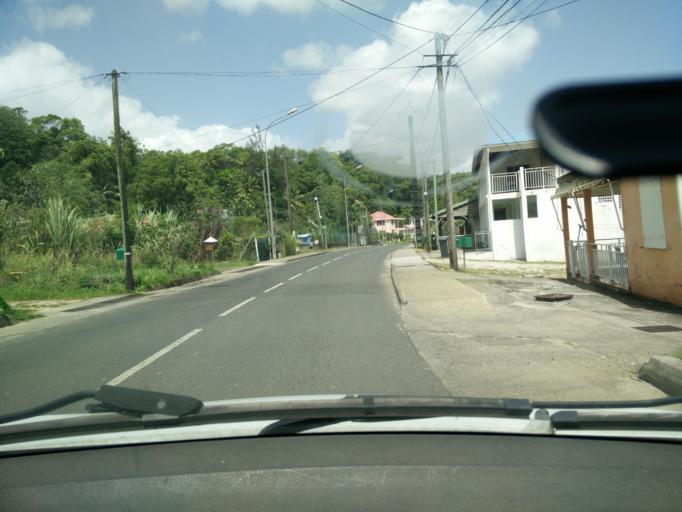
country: GP
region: Guadeloupe
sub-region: Guadeloupe
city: Les Abymes
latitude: 16.2887
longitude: -61.4742
